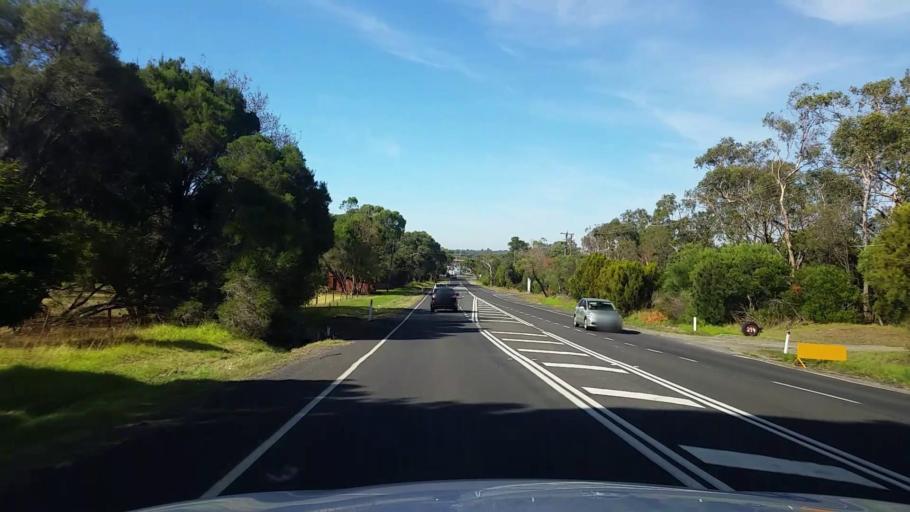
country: AU
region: Victoria
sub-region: Mornington Peninsula
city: Baxter
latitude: -38.1906
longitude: 145.1460
